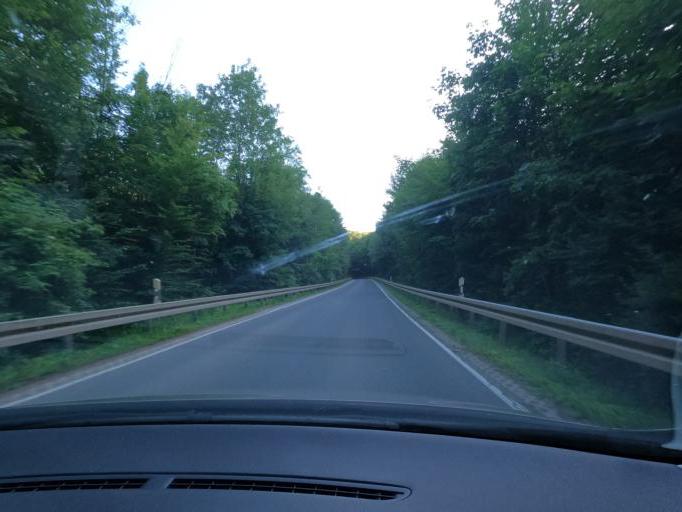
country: DE
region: Thuringia
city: Geisleden
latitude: 51.3774
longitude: 10.1993
